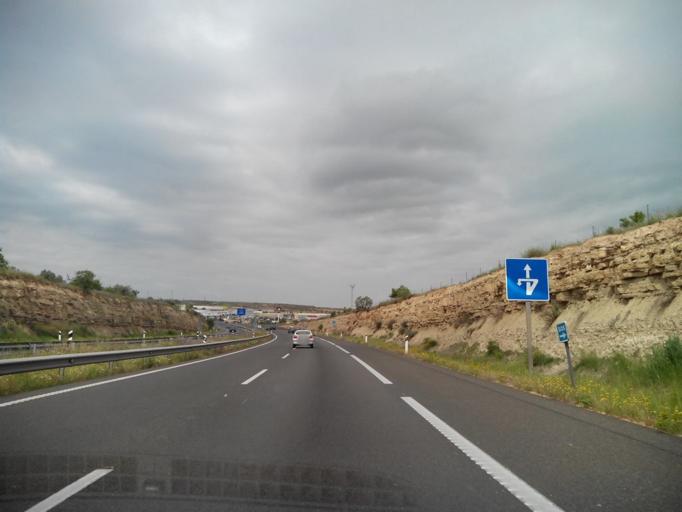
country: ES
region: Catalonia
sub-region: Provincia de Lleida
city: Tarrega
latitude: 41.6616
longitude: 1.1463
